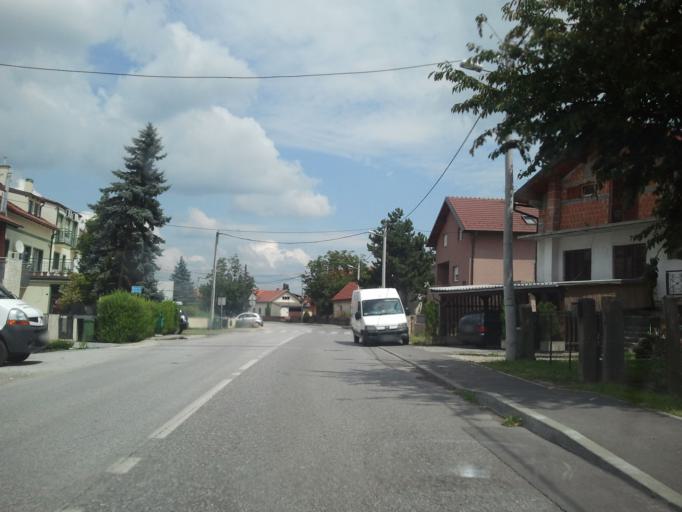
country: HR
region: Grad Zagreb
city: Zadvorsko
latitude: 45.7631
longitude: 15.9167
